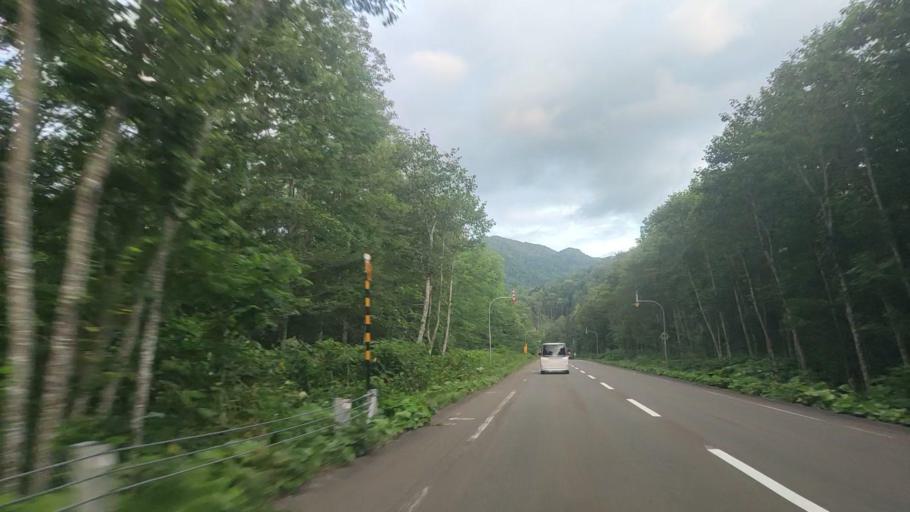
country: JP
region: Hokkaido
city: Ashibetsu
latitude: 43.3728
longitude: 142.2238
